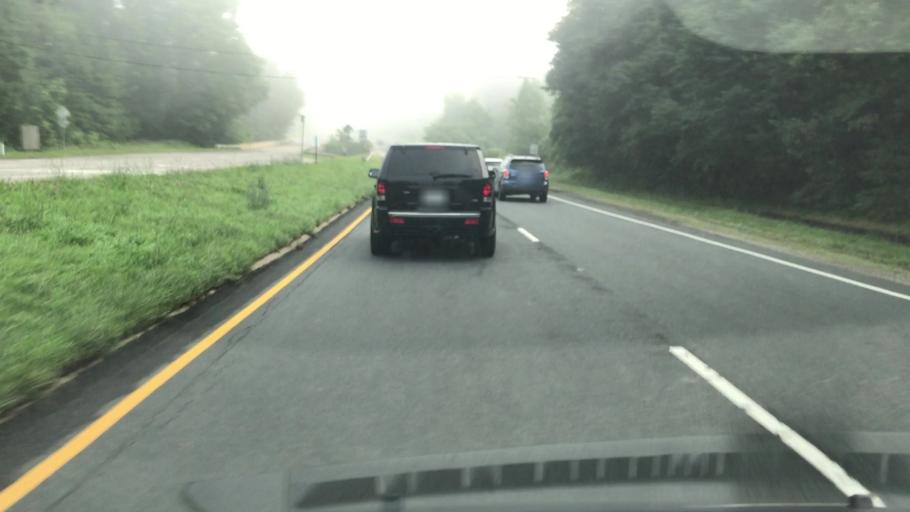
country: US
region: Virginia
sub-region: Fairfax County
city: Fairfax Station
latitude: 38.7993
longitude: -77.3253
